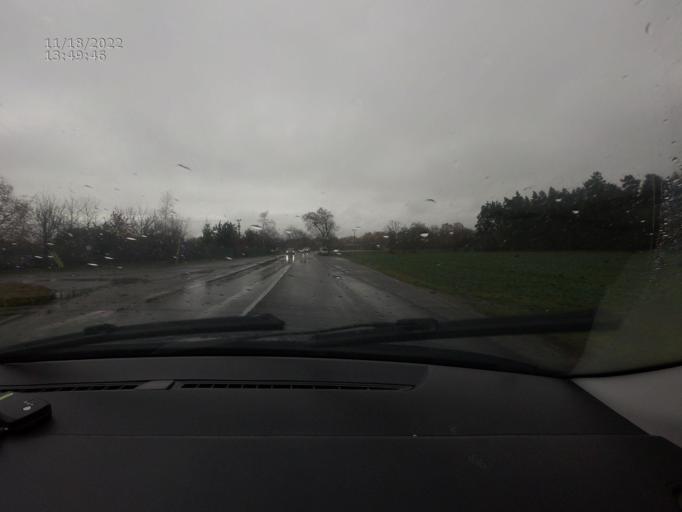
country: CZ
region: Jihocesky
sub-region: Okres Strakonice
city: Blatna
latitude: 49.4137
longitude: 13.9027
